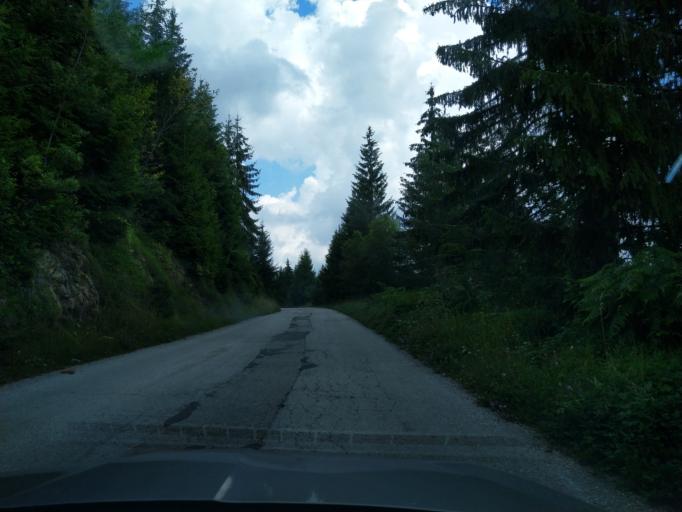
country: RS
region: Central Serbia
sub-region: Zlatiborski Okrug
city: Nova Varos
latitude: 43.5246
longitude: 19.8679
